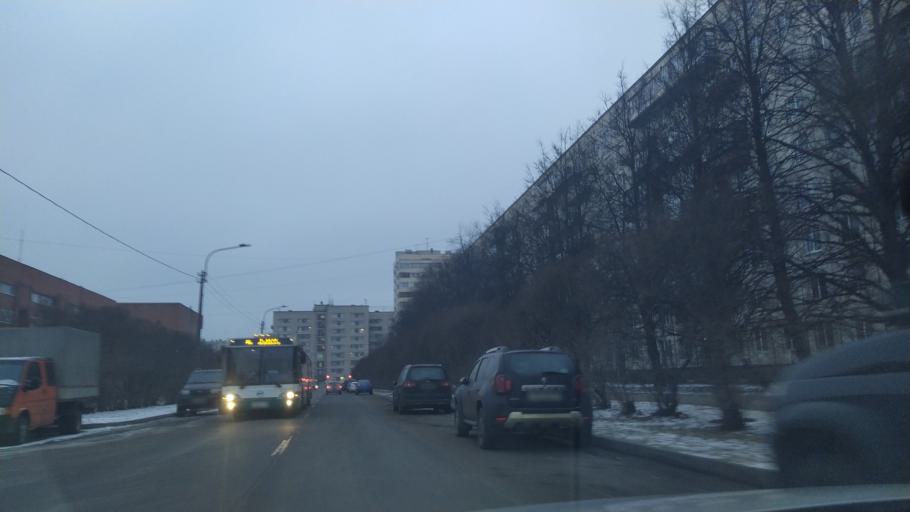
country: RU
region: St.-Petersburg
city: Grazhdanka
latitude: 60.0461
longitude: 30.3938
